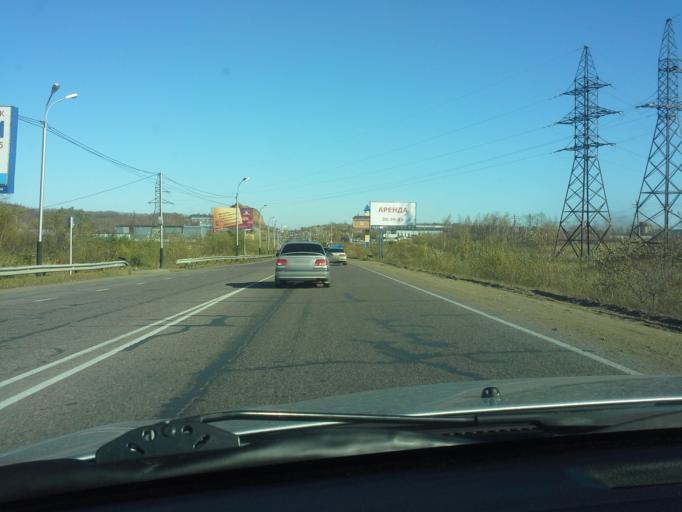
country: RU
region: Khabarovsk Krai
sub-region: Khabarovskiy Rayon
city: Khabarovsk
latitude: 48.5481
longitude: 135.0601
